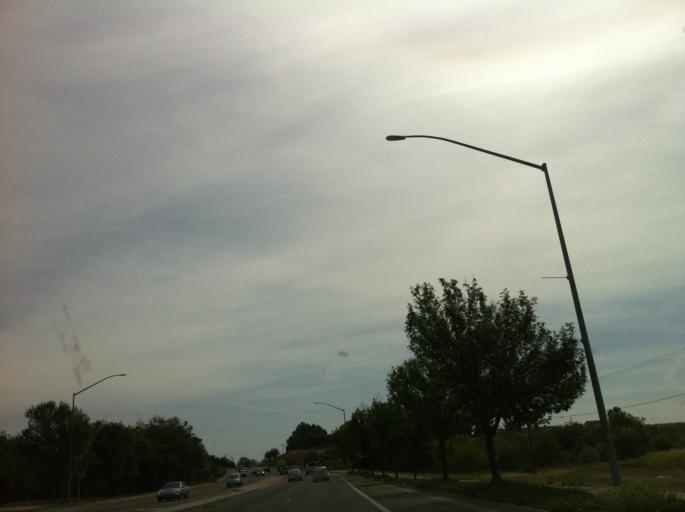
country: US
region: Oregon
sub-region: Malheur County
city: Ontario
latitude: 44.0247
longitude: -116.9408
